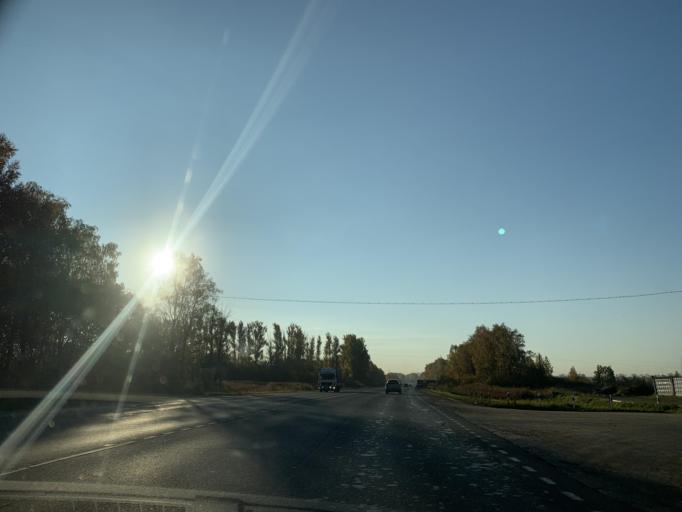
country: RU
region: Jaroslavl
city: Konstantinovskiy
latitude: 57.7390
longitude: 39.7297
